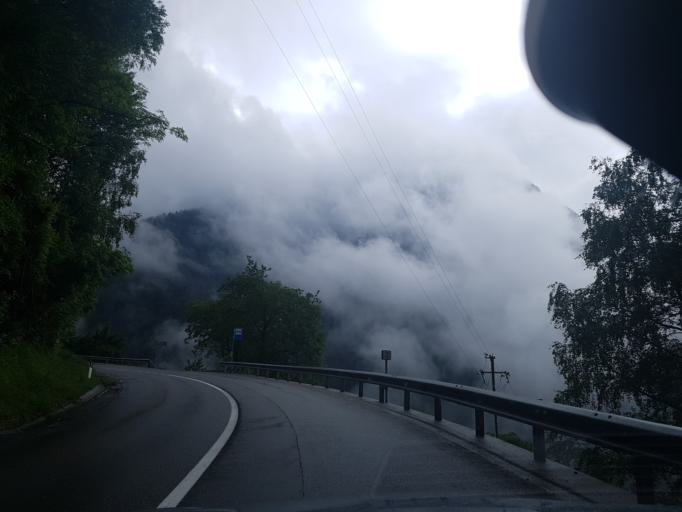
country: IT
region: Trentino-Alto Adige
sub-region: Bolzano
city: Laion
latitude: 46.5994
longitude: 11.6069
